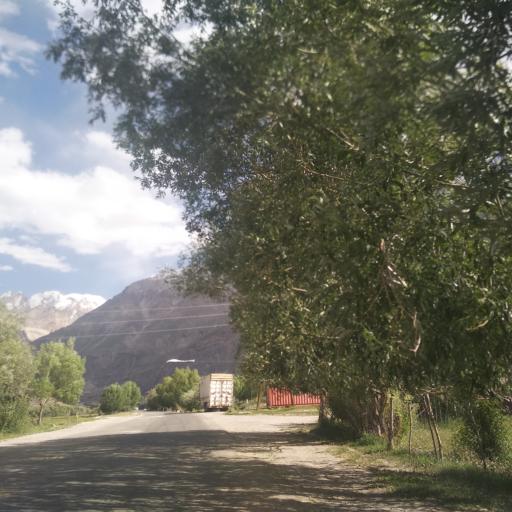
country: TJ
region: Gorno-Badakhshan
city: Roshtqal'a
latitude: 37.7246
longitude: 72.1613
